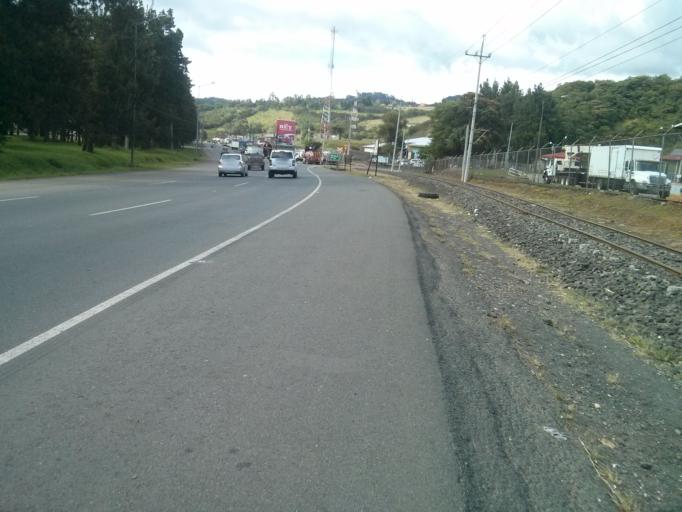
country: CR
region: Cartago
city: Cartago
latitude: 9.8962
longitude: -83.9433
